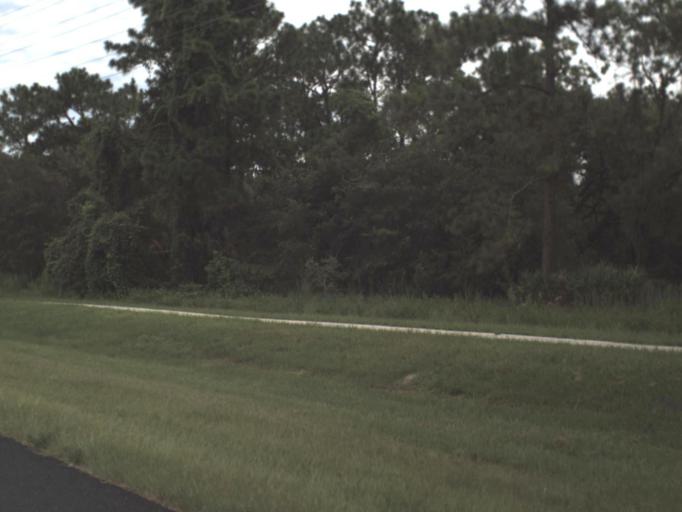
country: US
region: Florida
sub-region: Citrus County
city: Lecanto
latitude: 28.8747
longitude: -82.5188
